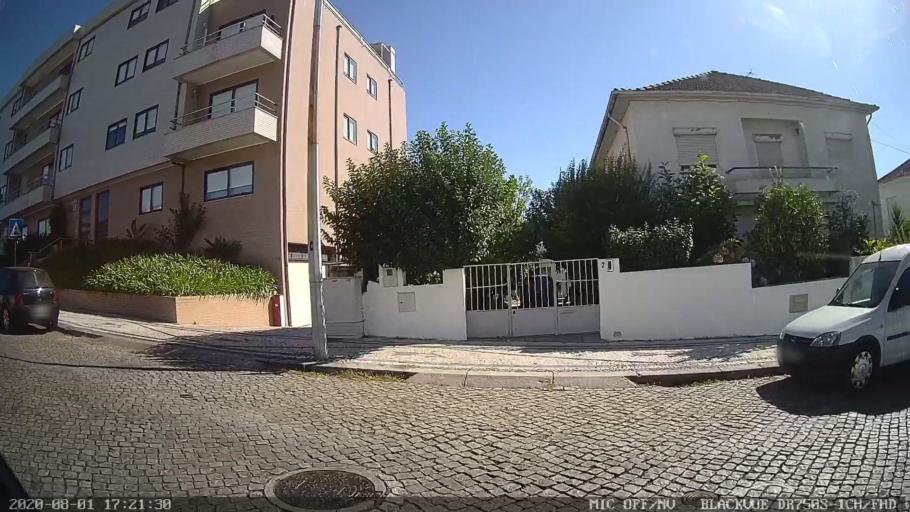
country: PT
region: Porto
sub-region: Santo Tirso
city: Santo Tirso
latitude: 41.3436
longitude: -8.4833
